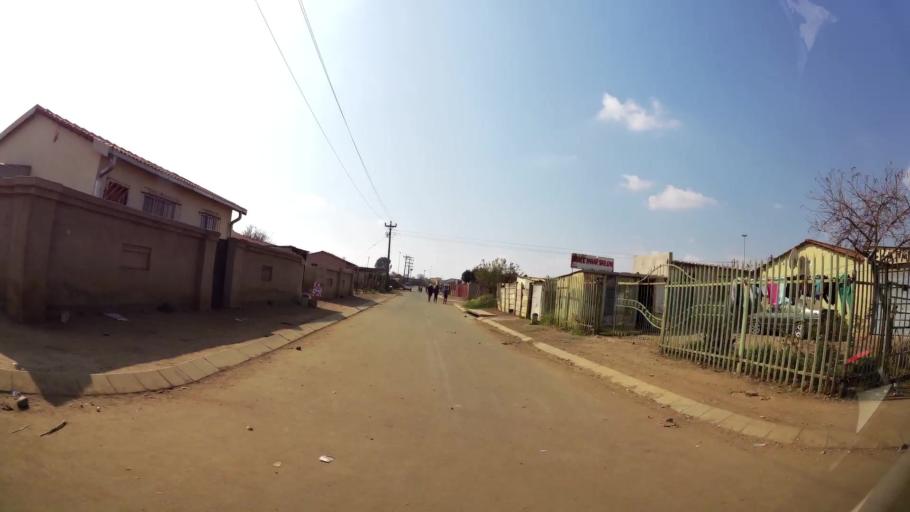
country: ZA
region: Gauteng
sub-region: Ekurhuleni Metropolitan Municipality
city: Springs
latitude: -26.1051
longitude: 28.4824
